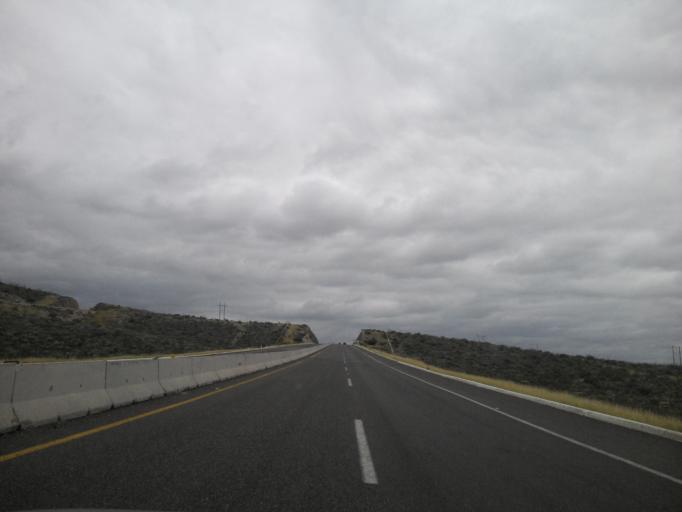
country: MX
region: Durango
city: Cuencame
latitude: 25.1489
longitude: -103.7489
